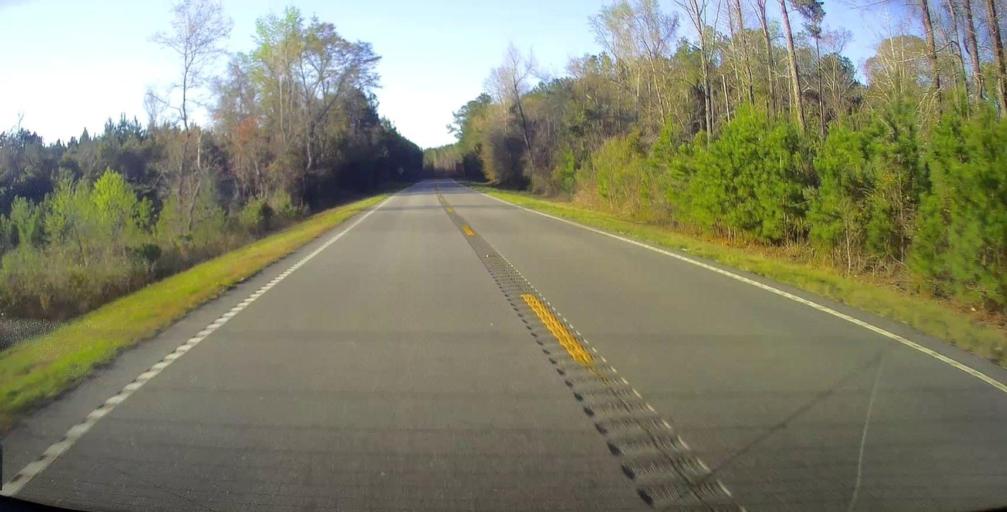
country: US
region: Georgia
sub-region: Pulaski County
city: Hawkinsville
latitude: 32.1931
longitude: -83.3697
